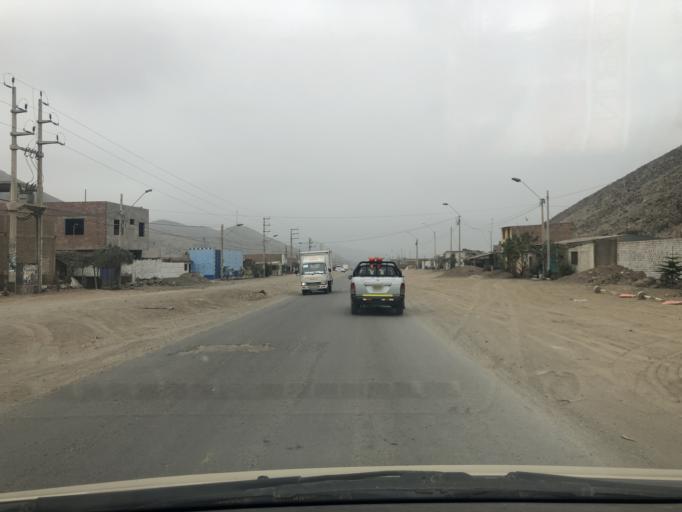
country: PE
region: Lima
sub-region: Lima
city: Cieneguilla
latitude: -12.1613
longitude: -76.8670
